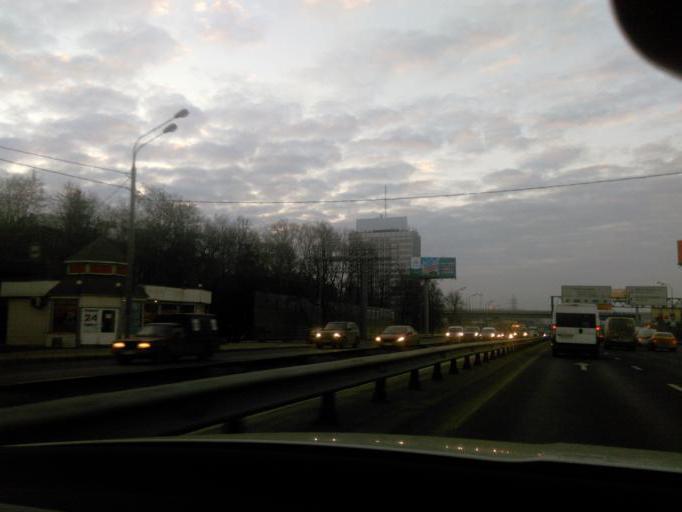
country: RU
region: Moscow
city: Khimki
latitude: 55.8853
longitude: 37.4404
